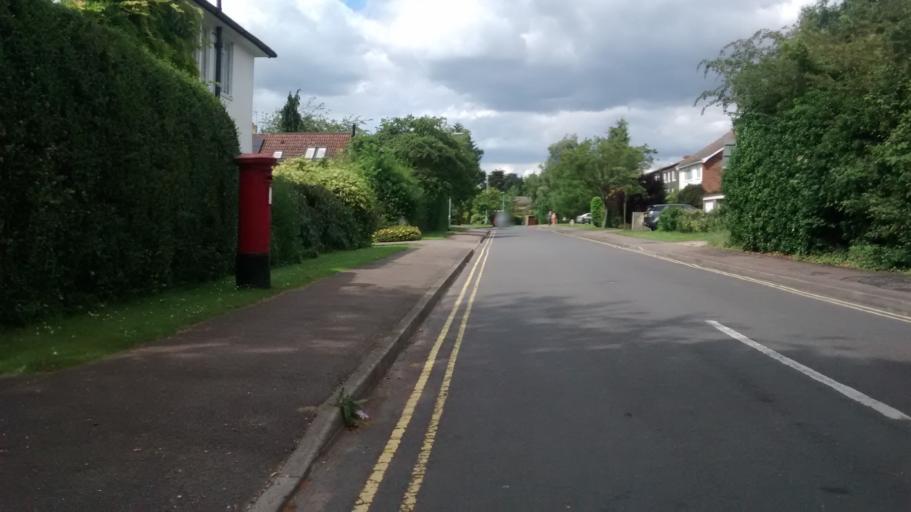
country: GB
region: England
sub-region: Cambridgeshire
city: Cambridge
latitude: 52.1982
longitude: 0.0980
